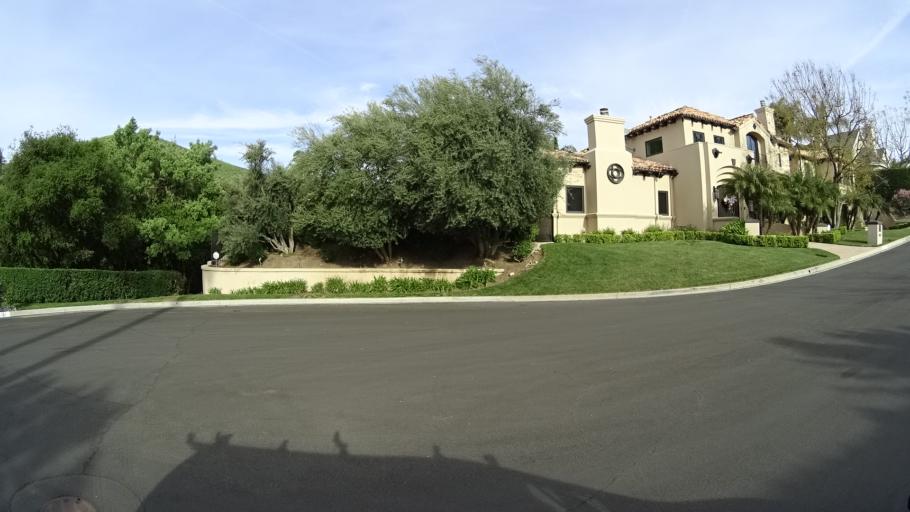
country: US
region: California
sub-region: Ventura County
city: Thousand Oaks
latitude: 34.1935
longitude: -118.8211
